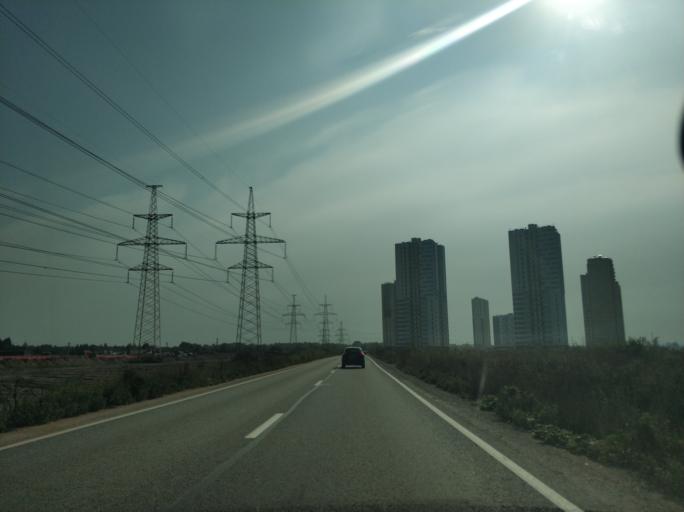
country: RU
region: St.-Petersburg
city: Krasnogvargeisky
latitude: 60.0144
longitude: 30.4771
